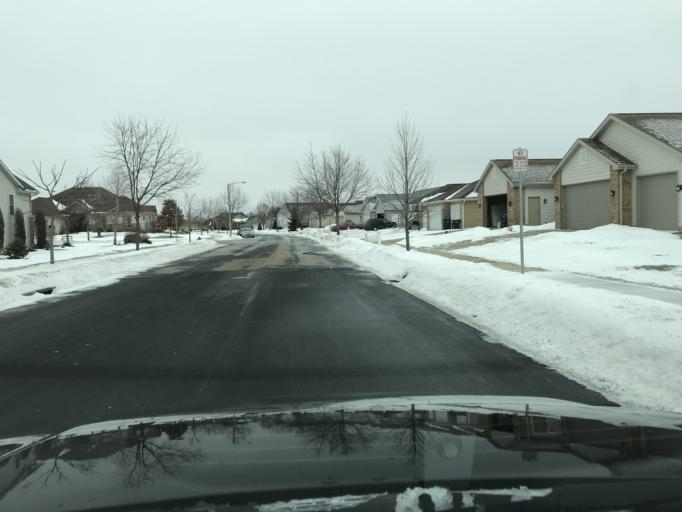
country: US
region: Wisconsin
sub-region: Dane County
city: Cottage Grove
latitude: 43.0909
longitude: -89.2198
